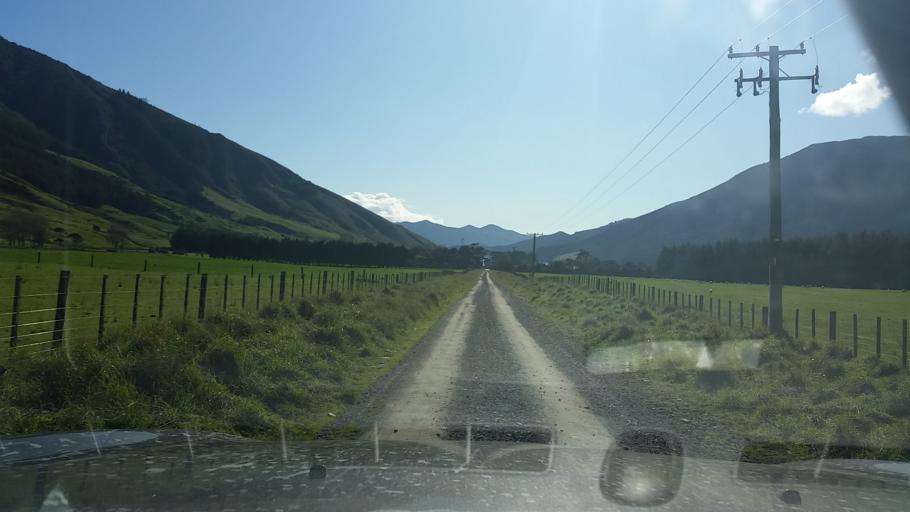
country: NZ
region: Marlborough
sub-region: Marlborough District
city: Picton
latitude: -41.1268
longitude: 174.0400
